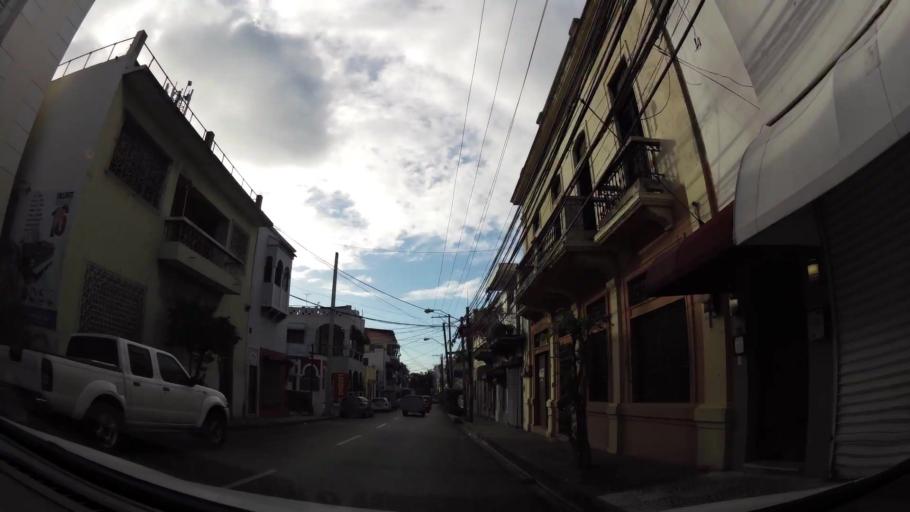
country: DO
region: Nacional
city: Ciudad Nueva
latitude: 18.4733
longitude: -69.8931
